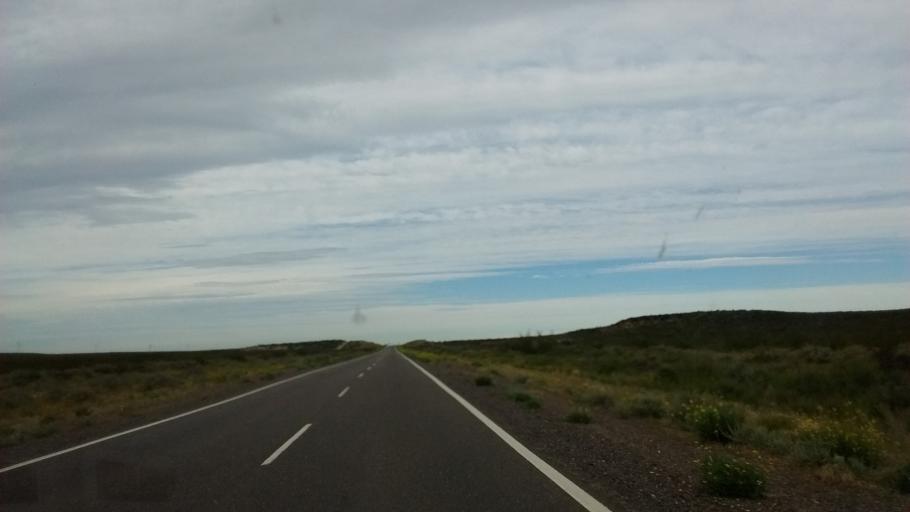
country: AR
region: Rio Negro
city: Contraalmirante Cordero
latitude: -38.4550
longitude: -68.0448
